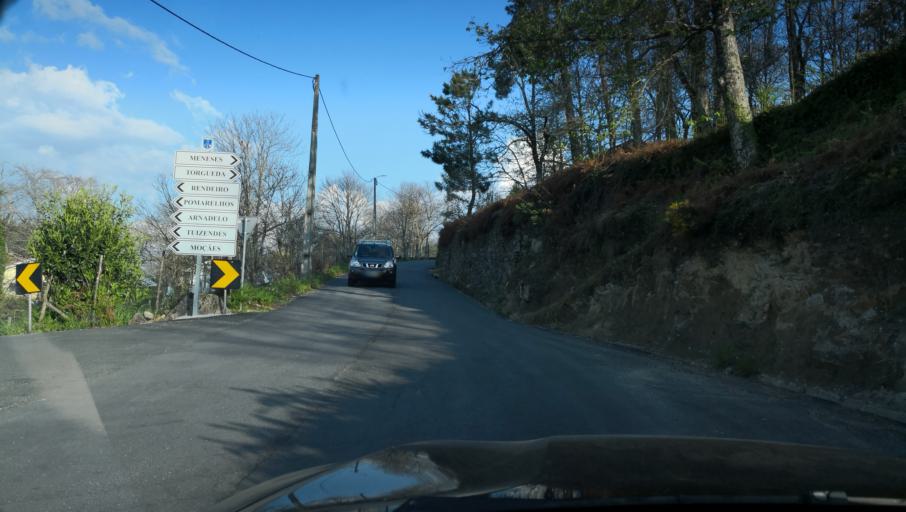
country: PT
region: Vila Real
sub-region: Santa Marta de Penaguiao
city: Santa Marta de Penaguiao
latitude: 41.2772
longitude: -7.8148
